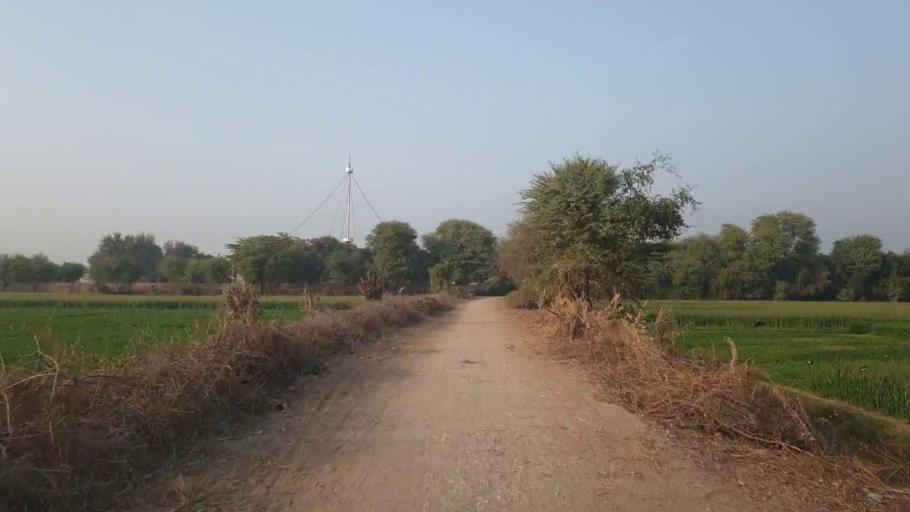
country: PK
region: Sindh
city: Bhit Shah
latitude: 25.8121
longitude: 68.4749
